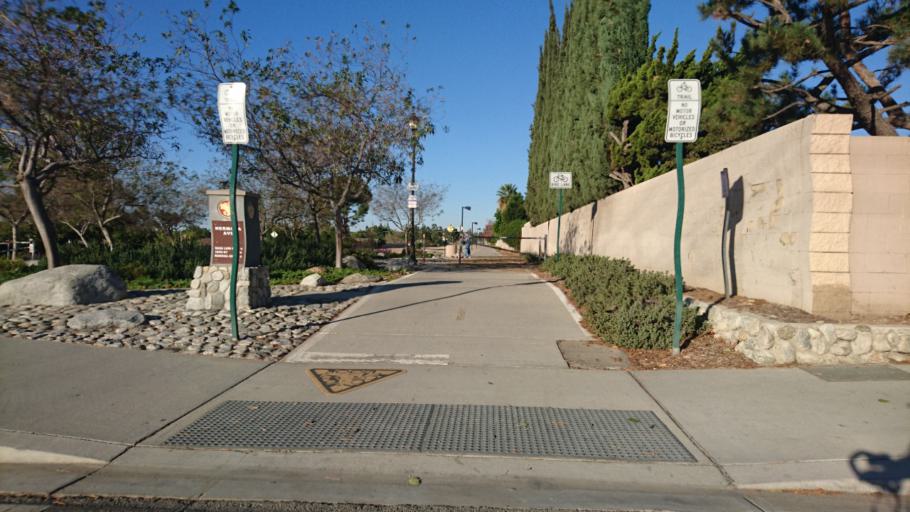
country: US
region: California
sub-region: San Bernardino County
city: Rancho Cucamonga
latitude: 34.1256
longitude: -117.5848
